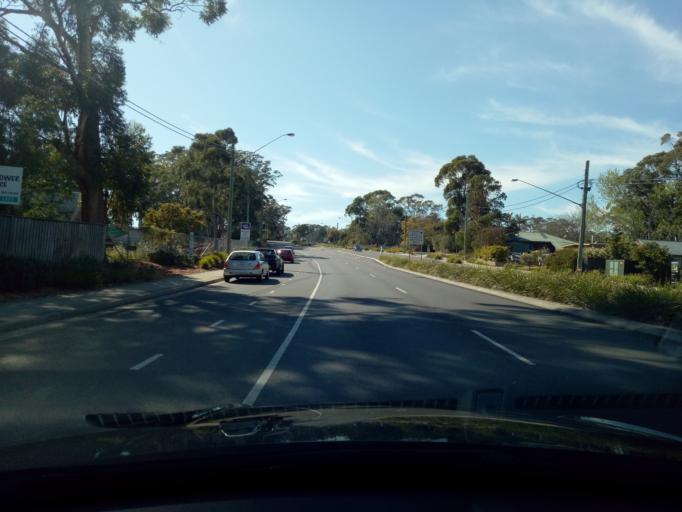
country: AU
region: New South Wales
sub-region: Gosford Shire
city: Erina
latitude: -33.4253
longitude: 151.4082
